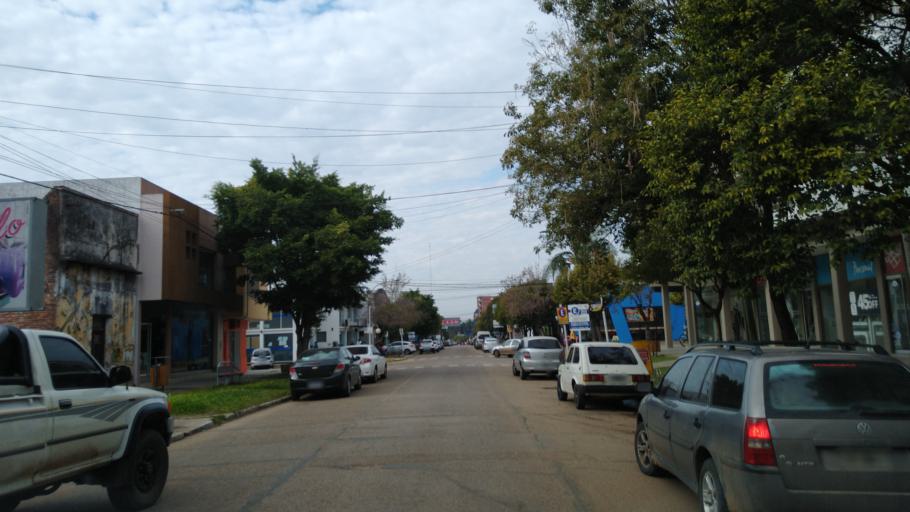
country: AR
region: Entre Rios
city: Chajari
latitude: -30.7595
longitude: -57.9841
